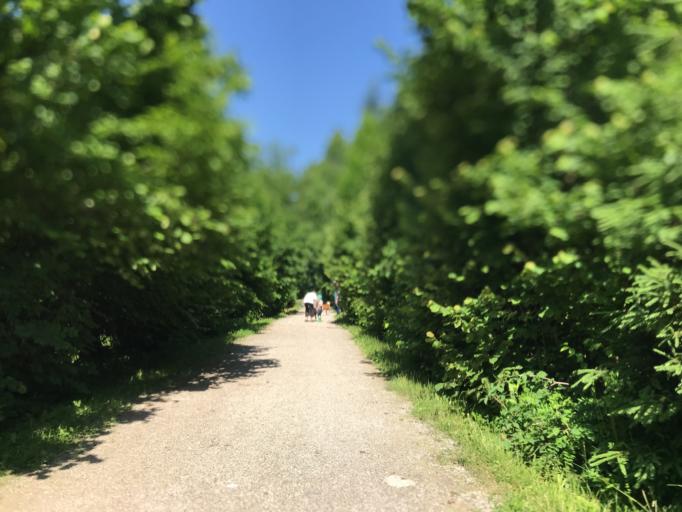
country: AT
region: Carinthia
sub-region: Villach Stadt
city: Villach
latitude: 46.5853
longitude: 13.8424
